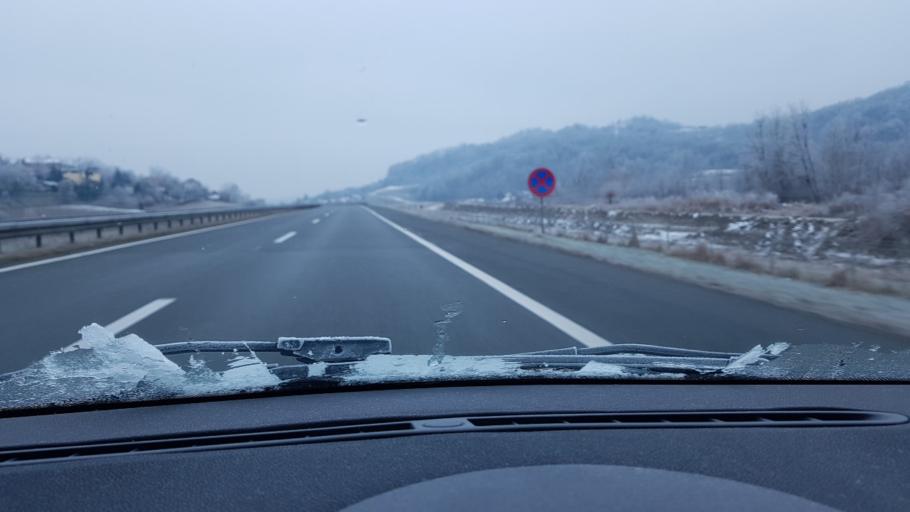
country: HR
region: Krapinsko-Zagorska
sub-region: Grad Krapina
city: Krapina
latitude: 46.1151
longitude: 15.8919
